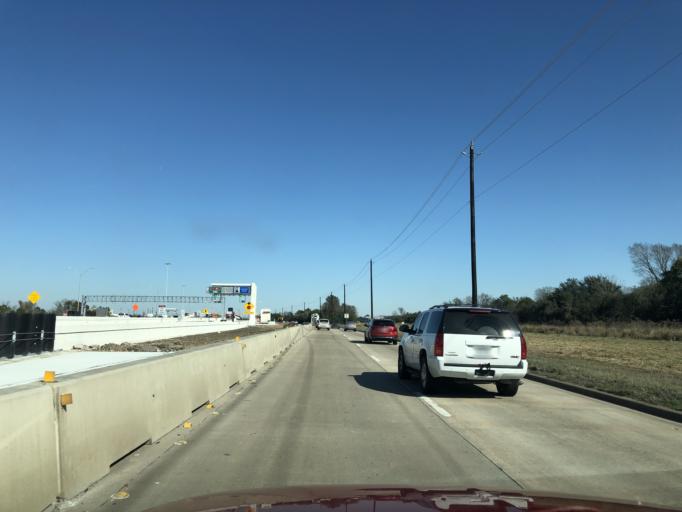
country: US
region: Texas
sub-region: Harris County
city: South Houston
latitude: 29.6258
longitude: -95.1748
